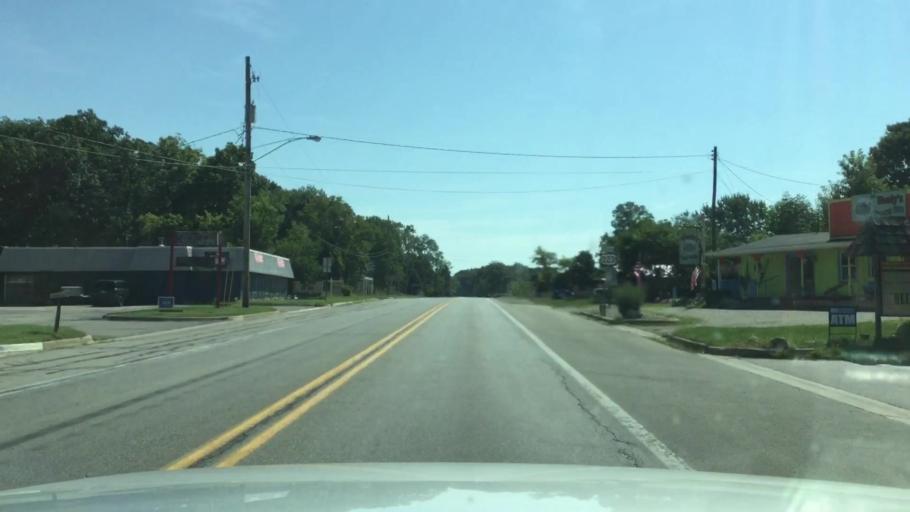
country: US
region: Michigan
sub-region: Lenawee County
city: Manitou Beach-Devils Lake
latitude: 42.0080
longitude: -84.2923
